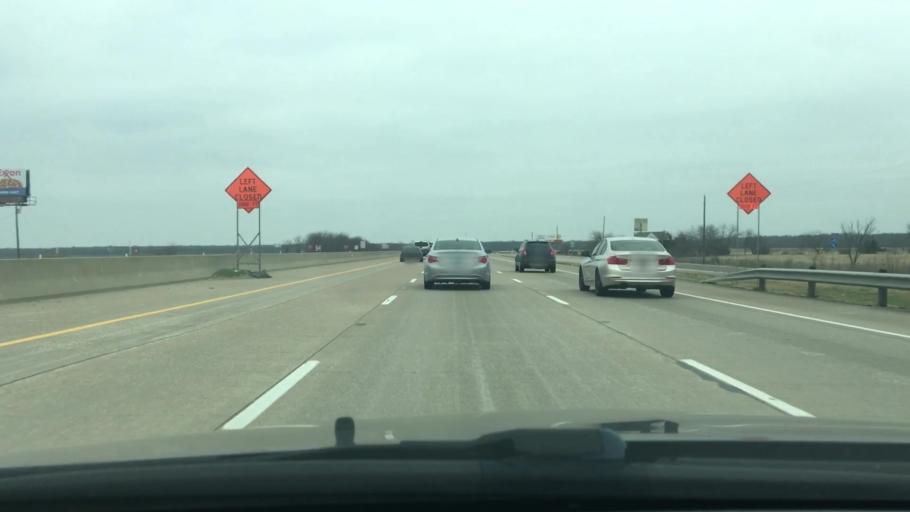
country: US
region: Texas
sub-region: Navarro County
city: Corsicana
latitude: 32.1790
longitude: -96.4713
